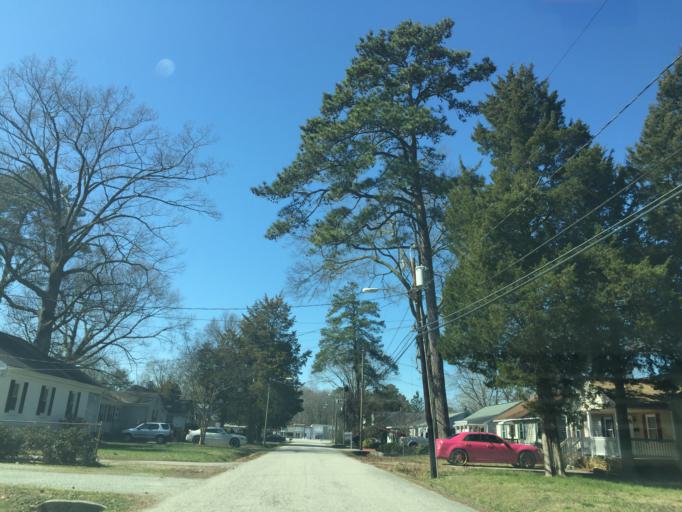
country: US
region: Virginia
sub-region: City of Newport News
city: Newport News
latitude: 37.0819
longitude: -76.4952
